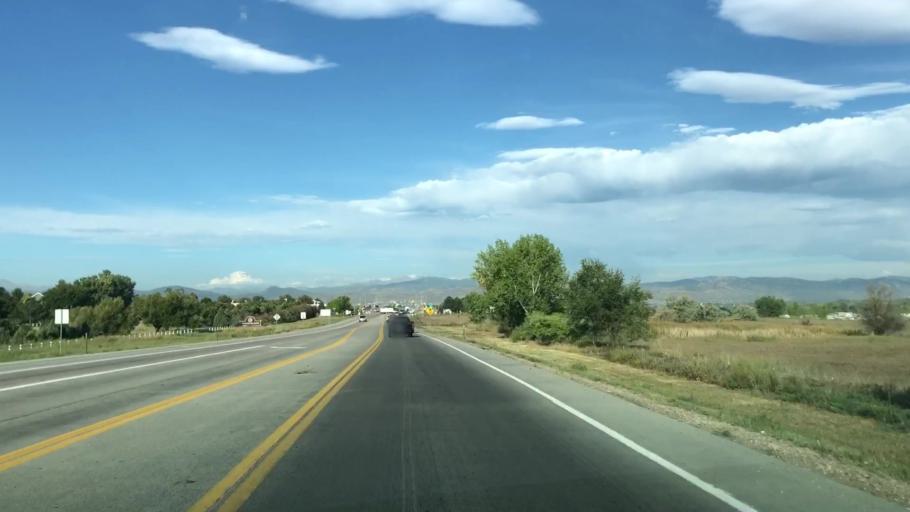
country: US
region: Colorado
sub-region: Weld County
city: Windsor
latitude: 40.4797
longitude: -104.9828
